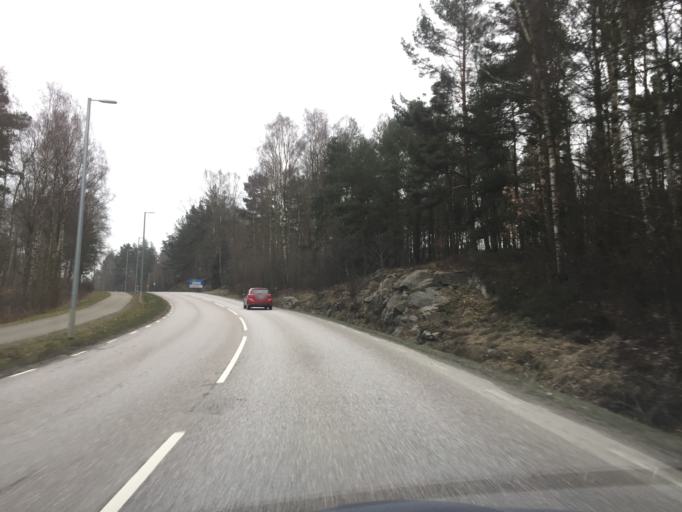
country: SE
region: Vaestra Goetaland
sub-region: Goteborg
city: Eriksbo
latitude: 57.7646
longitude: 12.0723
